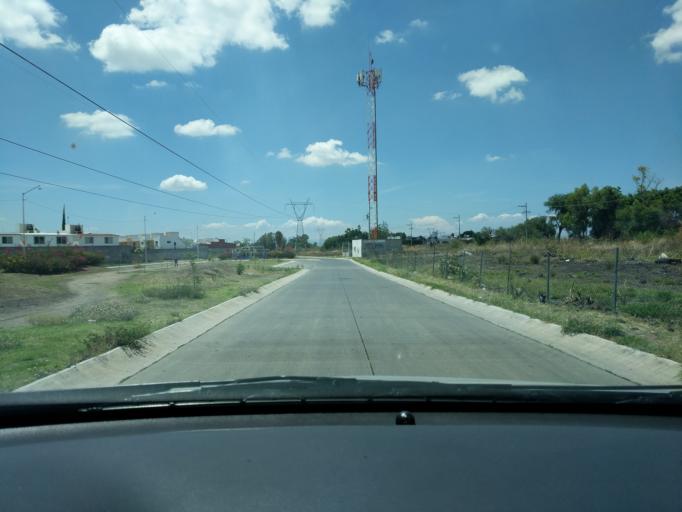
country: MX
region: Guanajuato
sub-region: Salamanca
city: El Divisador
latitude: 20.6027
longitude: -101.1756
